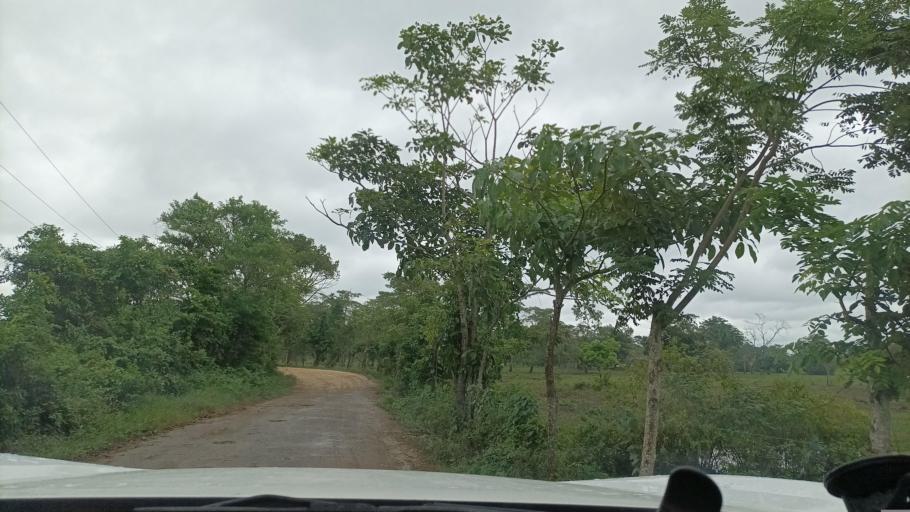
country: MX
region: Veracruz
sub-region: Moloacan
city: Cuichapa
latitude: 17.7830
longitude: -94.3890
